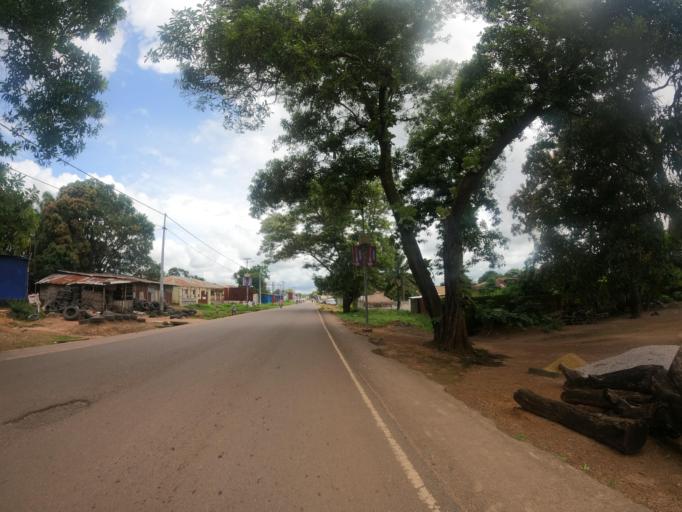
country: SL
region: Northern Province
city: Makeni
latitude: 8.8808
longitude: -12.0521
